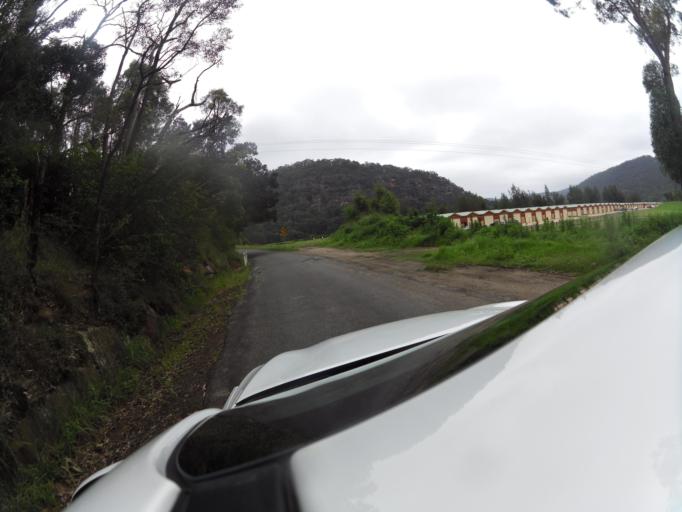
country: AU
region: New South Wales
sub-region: Hornsby Shire
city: Glenorie
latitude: -33.4041
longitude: 150.9753
